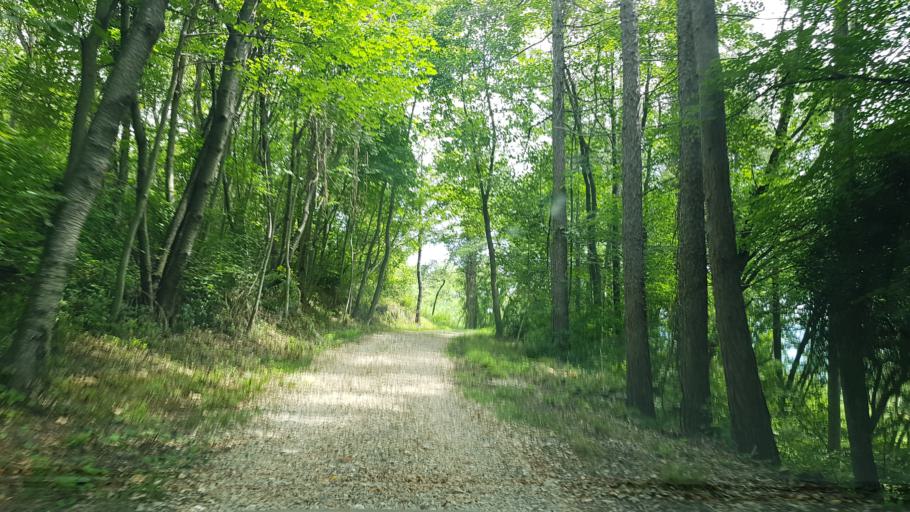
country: SI
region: Nova Gorica
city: Solkan
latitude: 46.0159
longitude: 13.6430
